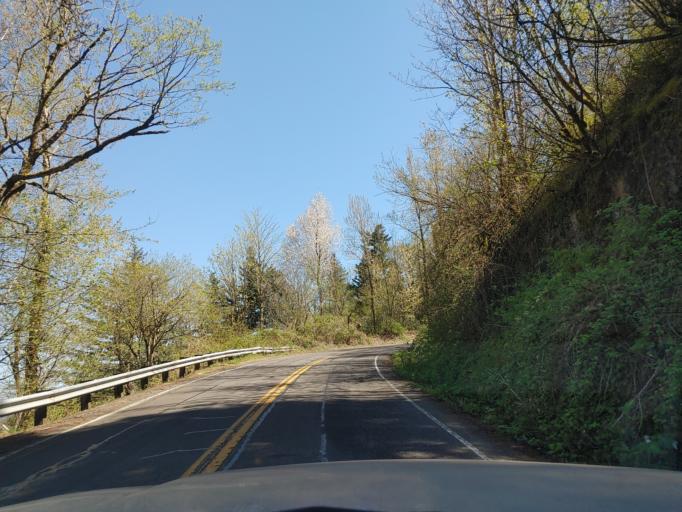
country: US
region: Washington
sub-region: Clark County
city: Washougal
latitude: 45.5393
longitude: -122.2850
